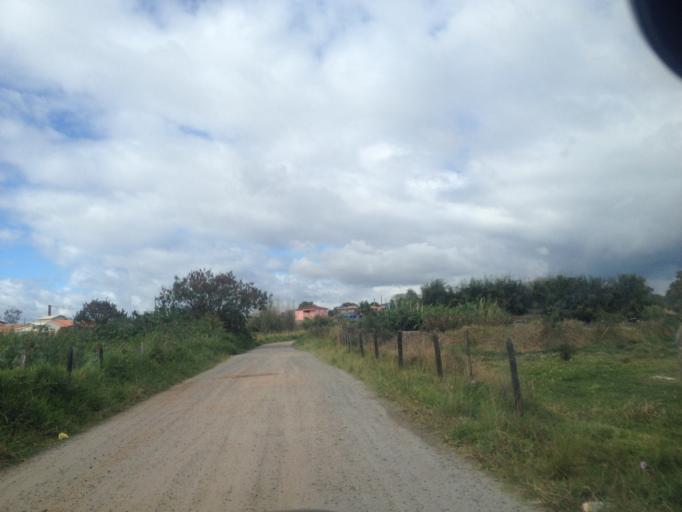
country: BR
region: Rio de Janeiro
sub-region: Porto Real
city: Porto Real
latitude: -22.4051
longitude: -44.2975
